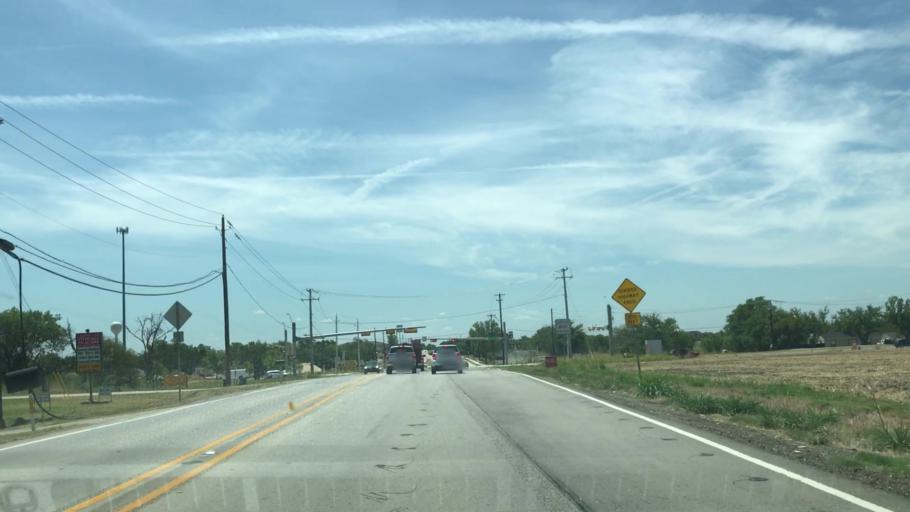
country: US
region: Texas
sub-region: Collin County
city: Saint Paul
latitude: 33.0559
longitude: -96.5684
